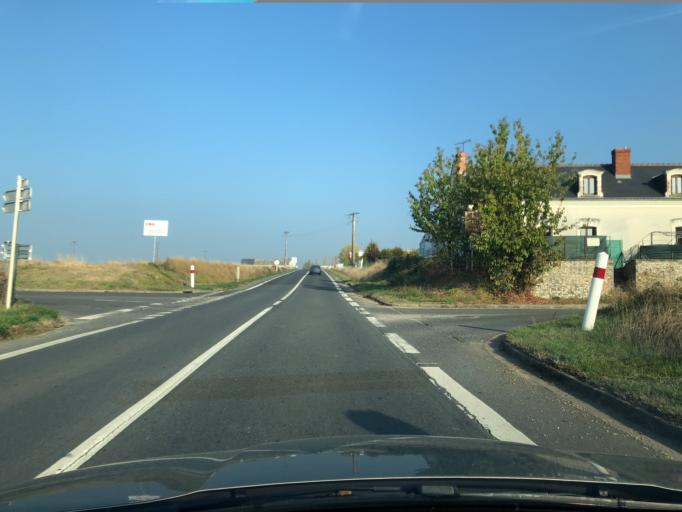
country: FR
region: Centre
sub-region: Departement d'Indre-et-Loire
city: Chanceaux-sur-Choisille
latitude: 47.4571
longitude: 0.6942
